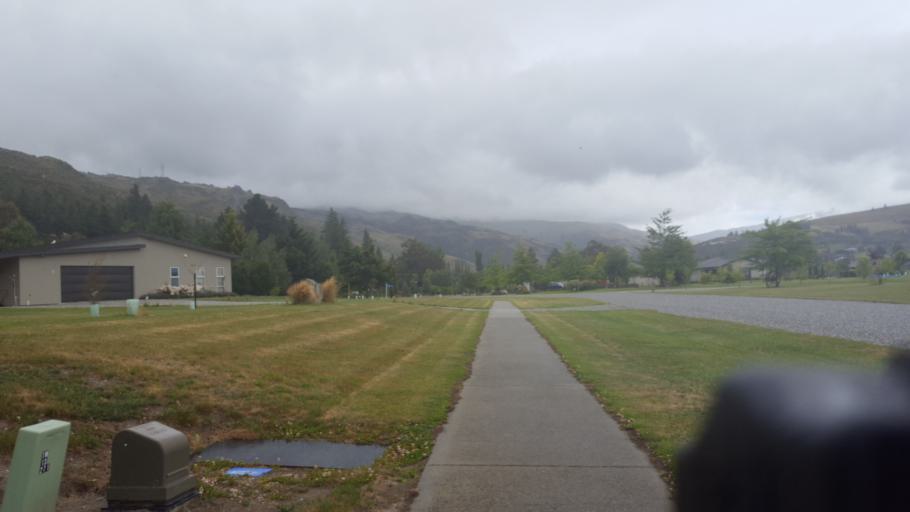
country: NZ
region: Otago
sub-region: Queenstown-Lakes District
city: Wanaka
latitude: -45.1958
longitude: 169.3164
